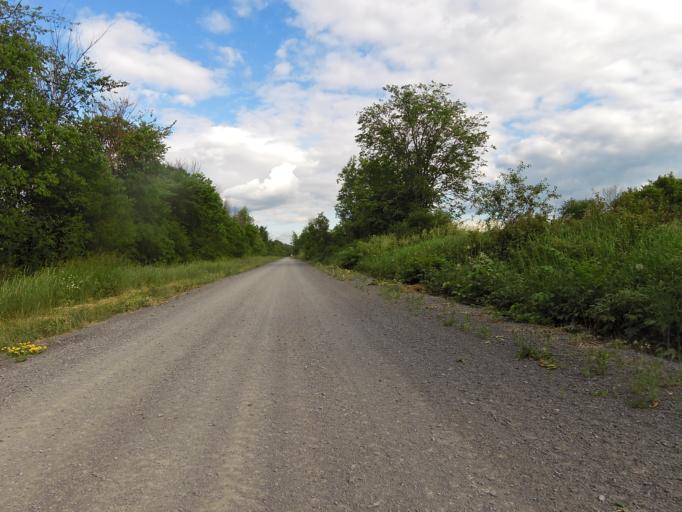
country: CA
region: Ontario
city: Arnprior
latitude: 45.3058
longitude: -76.2723
